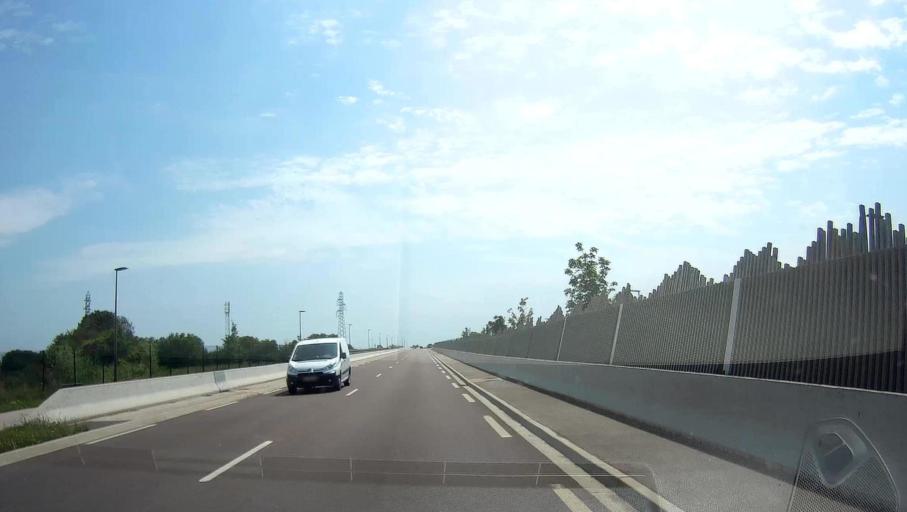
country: FR
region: Bourgogne
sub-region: Departement de la Cote-d'Or
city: Beaune
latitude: 47.0350
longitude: 4.8551
